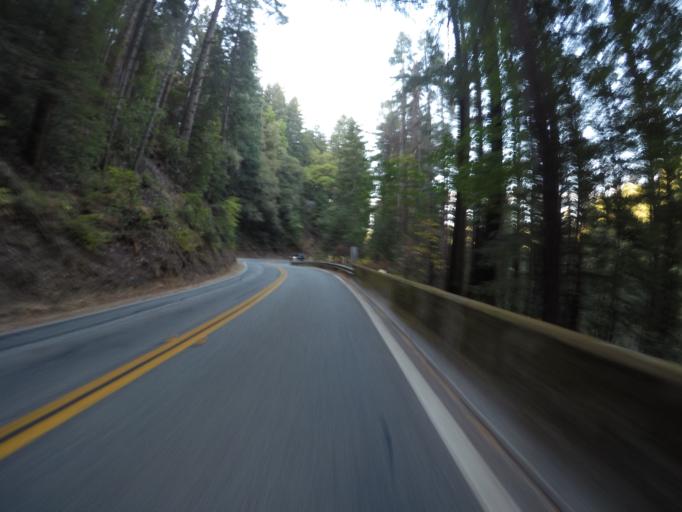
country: US
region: California
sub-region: Santa Cruz County
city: Mount Hermon
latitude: 37.0277
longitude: -122.0588
